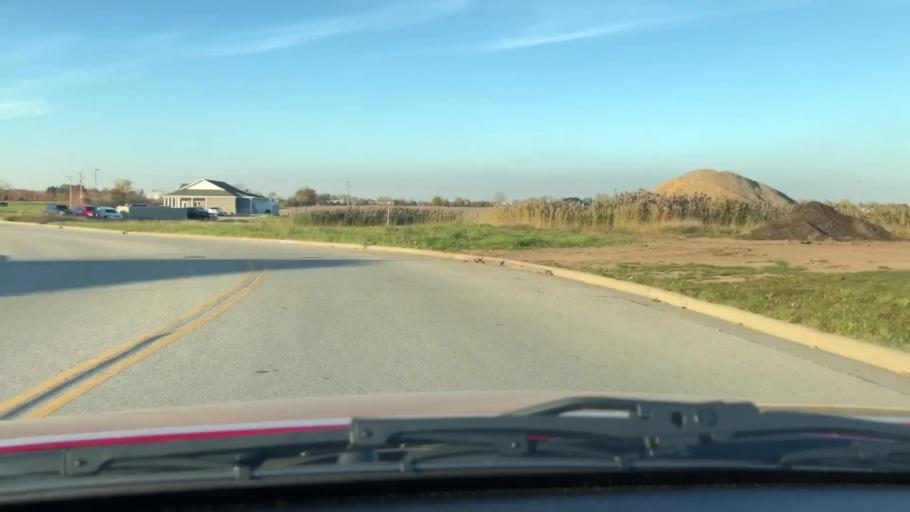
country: US
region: Wisconsin
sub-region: Brown County
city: De Pere
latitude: 44.4435
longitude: -88.1253
